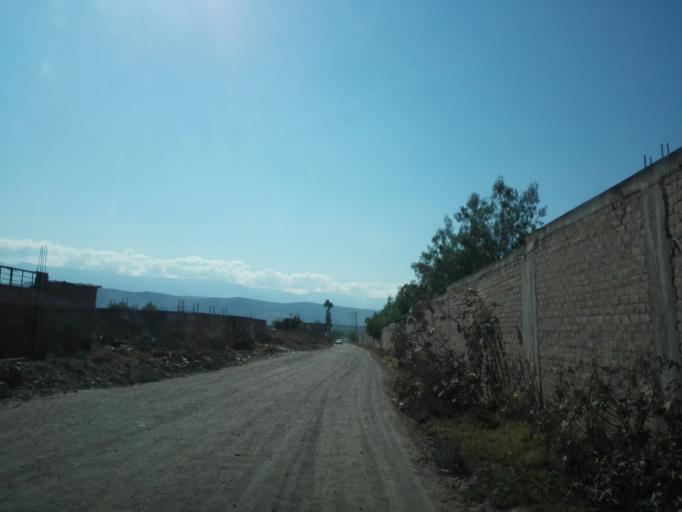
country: PE
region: Ayacucho
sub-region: Provincia de Huamanga
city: Ayacucho
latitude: -13.1599
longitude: -74.2030
